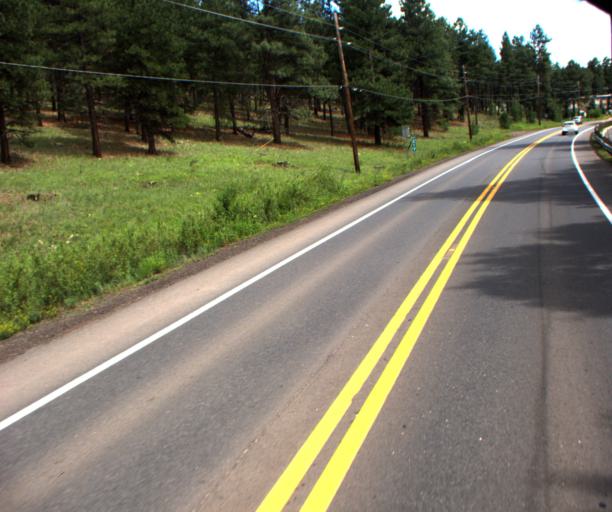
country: US
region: Arizona
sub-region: Coconino County
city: Flagstaff
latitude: 35.2197
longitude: -111.6512
